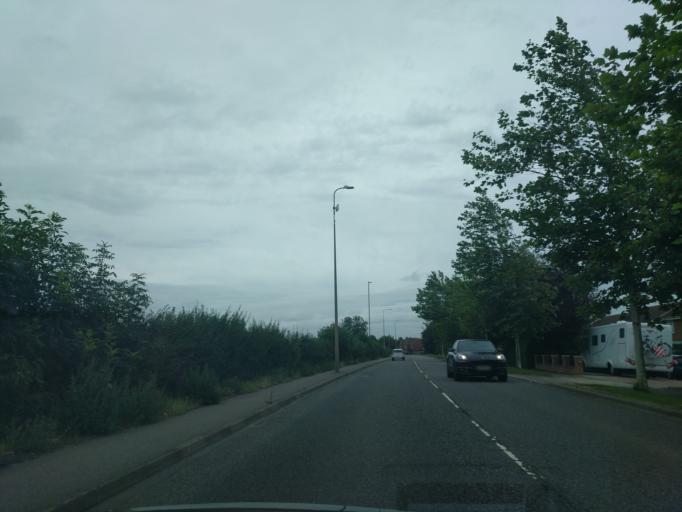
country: GB
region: England
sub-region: Lincolnshire
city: Great Gonerby
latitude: 52.9181
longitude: -0.6728
